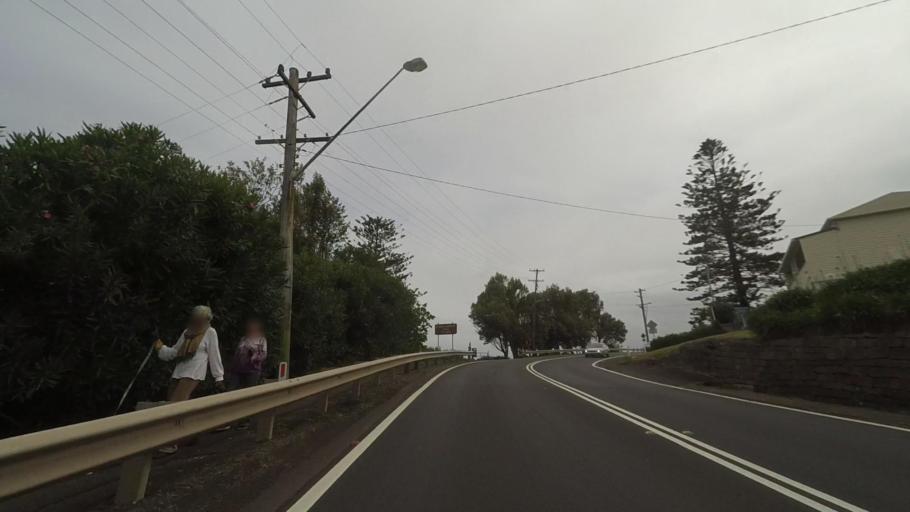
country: AU
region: New South Wales
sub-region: Wollongong
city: Bulli
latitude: -34.2800
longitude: 150.9538
